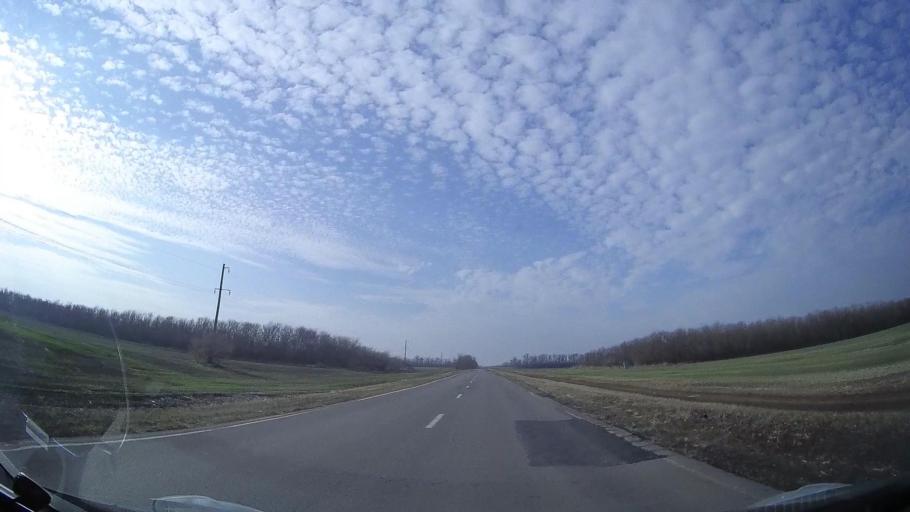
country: RU
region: Rostov
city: Veselyy
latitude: 46.9702
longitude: 40.7131
